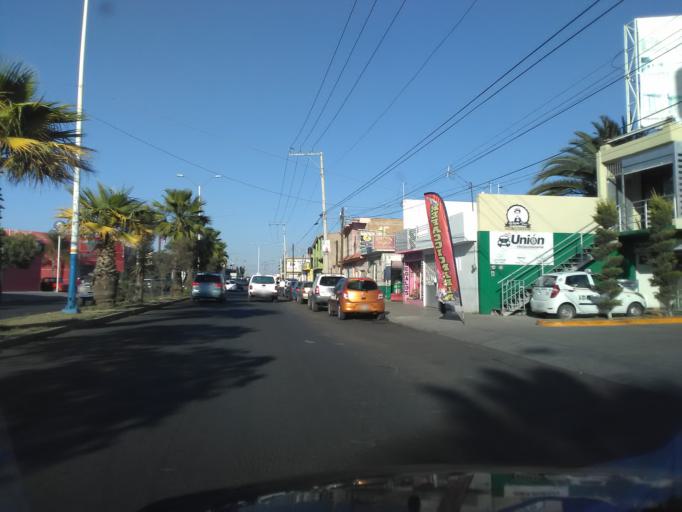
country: MX
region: Durango
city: Victoria de Durango
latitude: 24.0084
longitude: -104.6402
